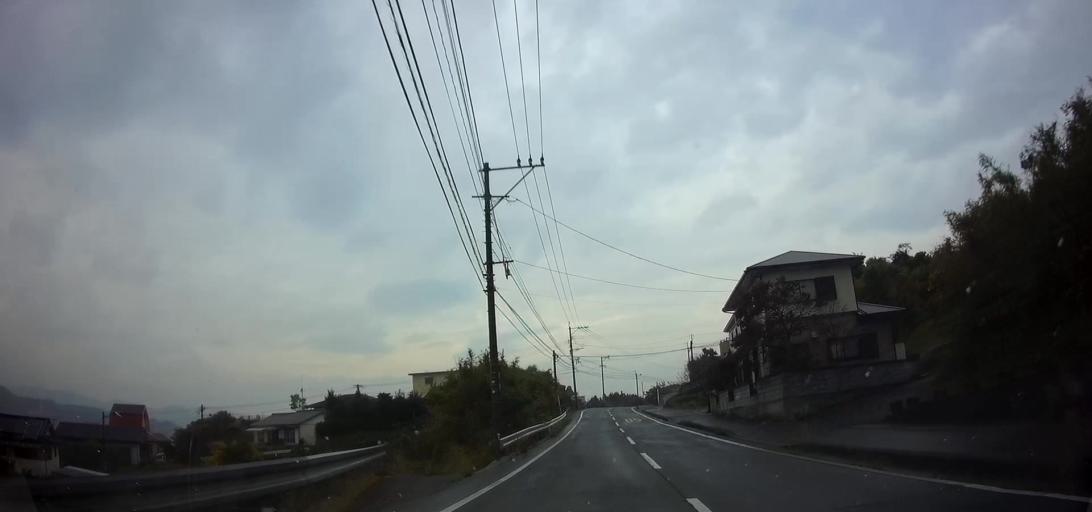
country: JP
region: Nagasaki
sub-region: Isahaya-shi
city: Isahaya
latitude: 32.8490
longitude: 129.9953
